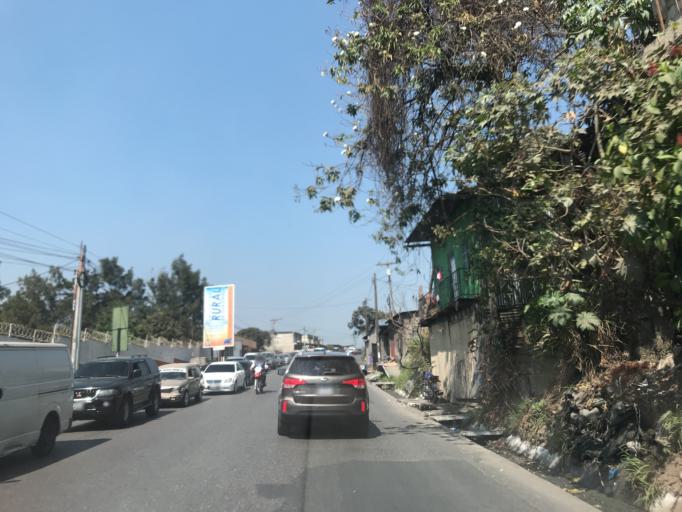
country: GT
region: Guatemala
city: Villa Nueva
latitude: 14.5405
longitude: -90.5571
